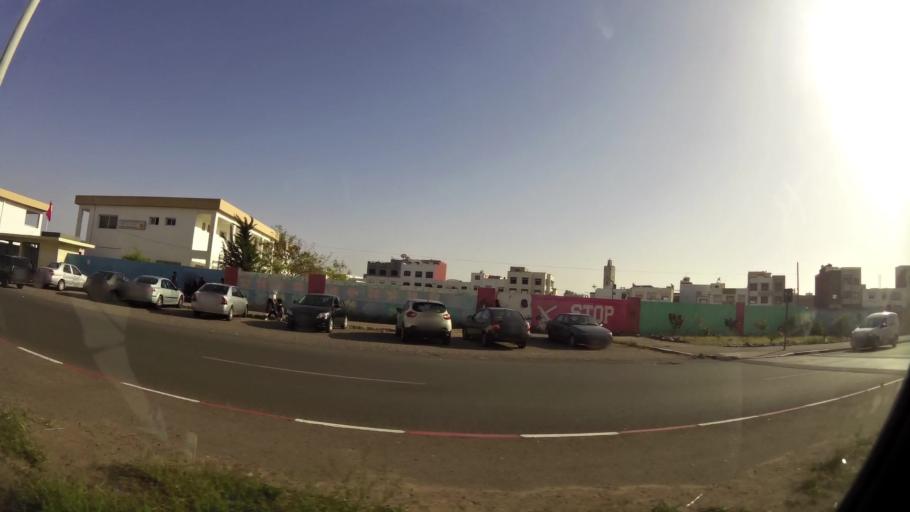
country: MA
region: Oued ed Dahab-Lagouira
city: Dakhla
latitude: 30.3960
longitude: -9.5435
